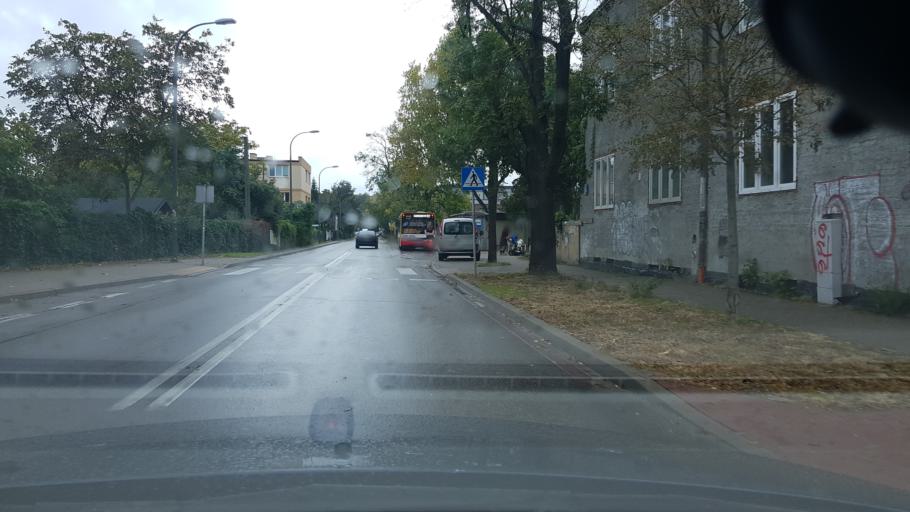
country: PL
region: Masovian Voivodeship
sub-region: Warszawa
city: Zoliborz
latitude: 52.2818
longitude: 20.9727
